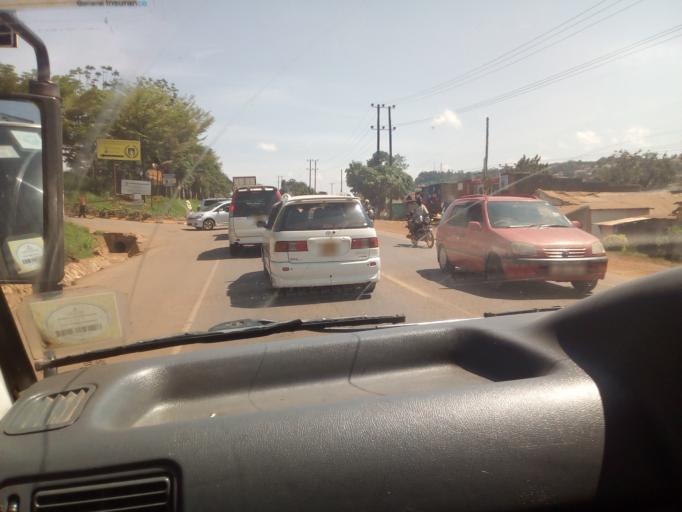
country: UG
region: Central Region
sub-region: Wakiso District
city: Kajansi
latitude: 0.2461
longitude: 32.5582
